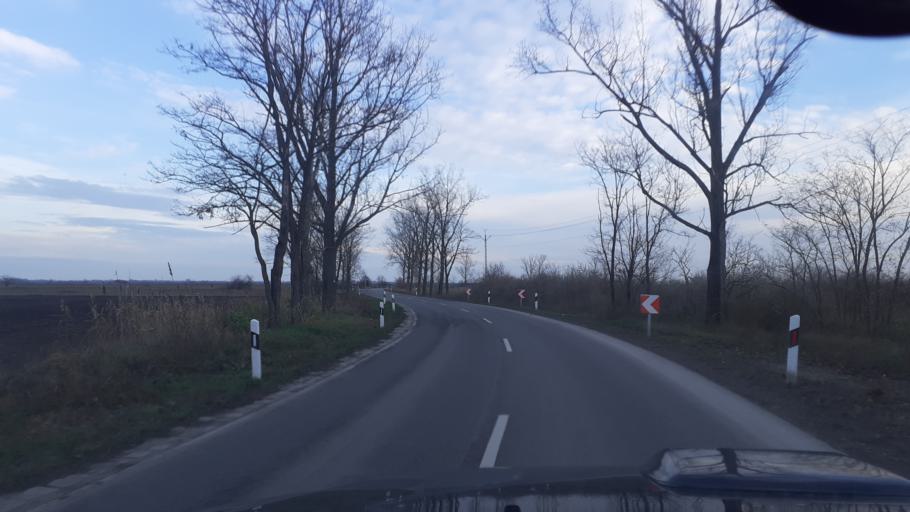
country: HU
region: Bacs-Kiskun
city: Kunszentmiklos
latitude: 47.0006
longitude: 19.1299
